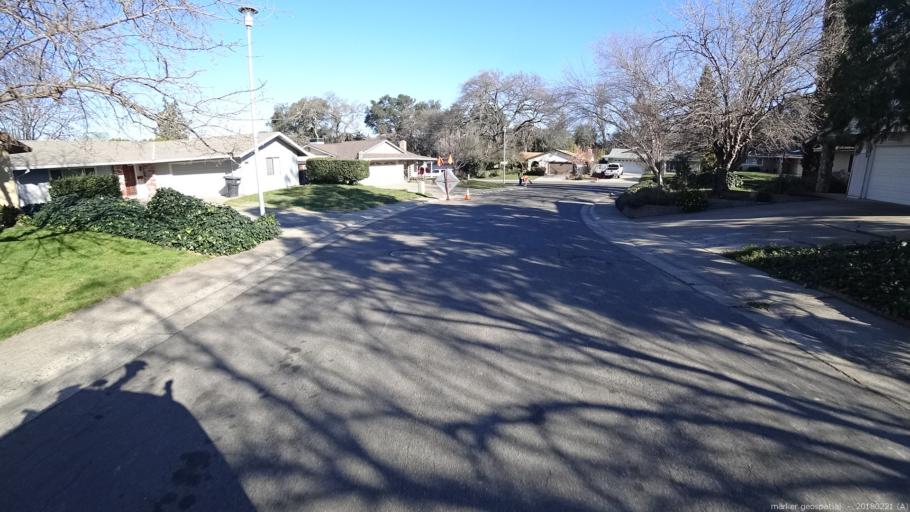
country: US
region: California
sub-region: Sacramento County
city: Orangevale
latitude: 38.6834
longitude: -121.2481
